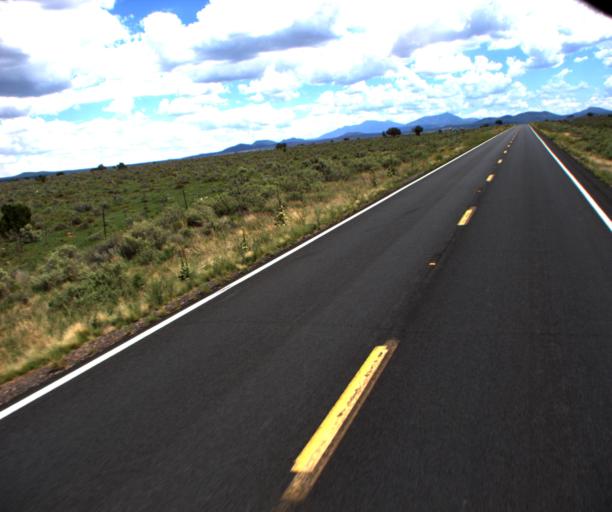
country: US
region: Arizona
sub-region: Coconino County
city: Williams
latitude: 35.6335
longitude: -112.1203
